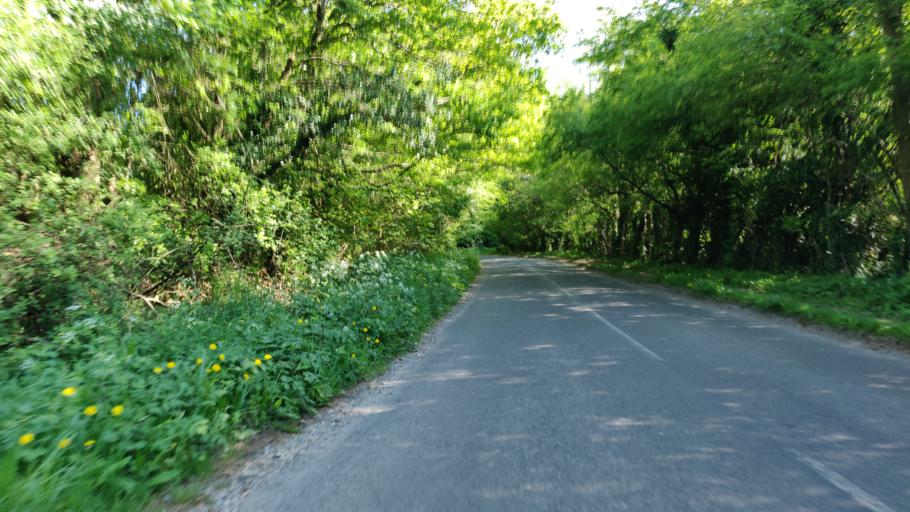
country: GB
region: England
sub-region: West Sussex
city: Southwater
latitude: 51.0282
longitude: -0.3795
